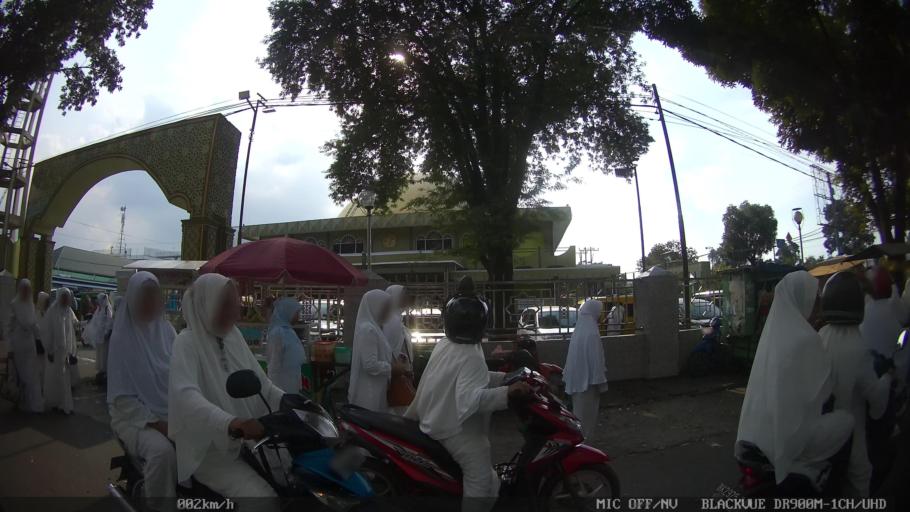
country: ID
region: North Sumatra
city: Binjai
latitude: 3.6081
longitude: 98.4978
